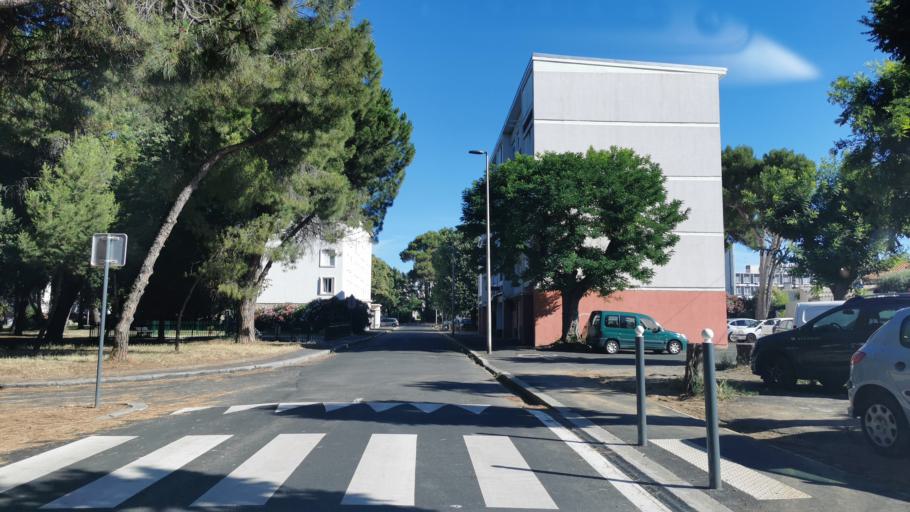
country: FR
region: Languedoc-Roussillon
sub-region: Departement de l'Herault
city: Beziers
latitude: 43.3436
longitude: 3.2368
